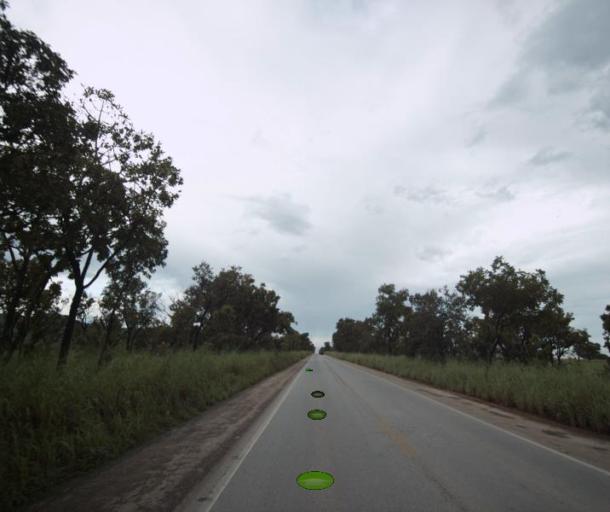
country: BR
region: Goias
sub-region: Porangatu
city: Porangatu
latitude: -13.6112
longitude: -49.0423
